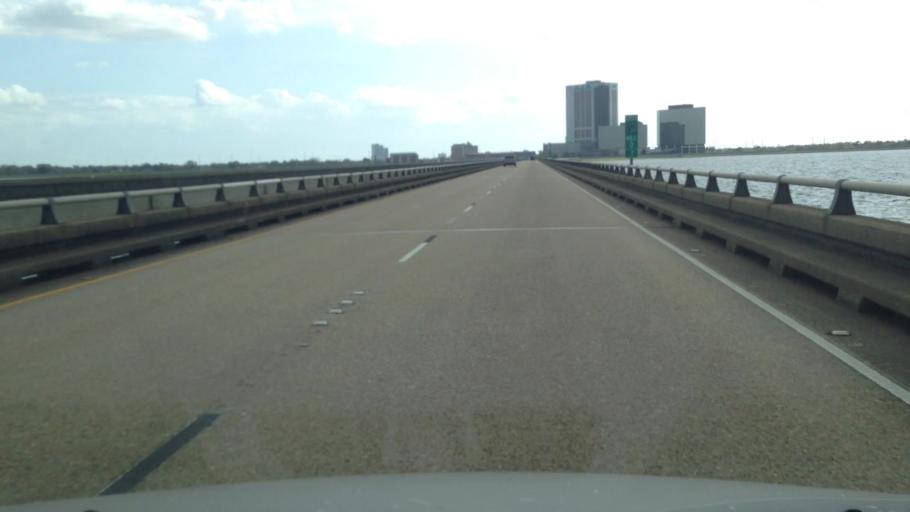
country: US
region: Louisiana
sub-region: Jefferson Parish
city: Metairie
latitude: 30.0320
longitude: -90.1523
